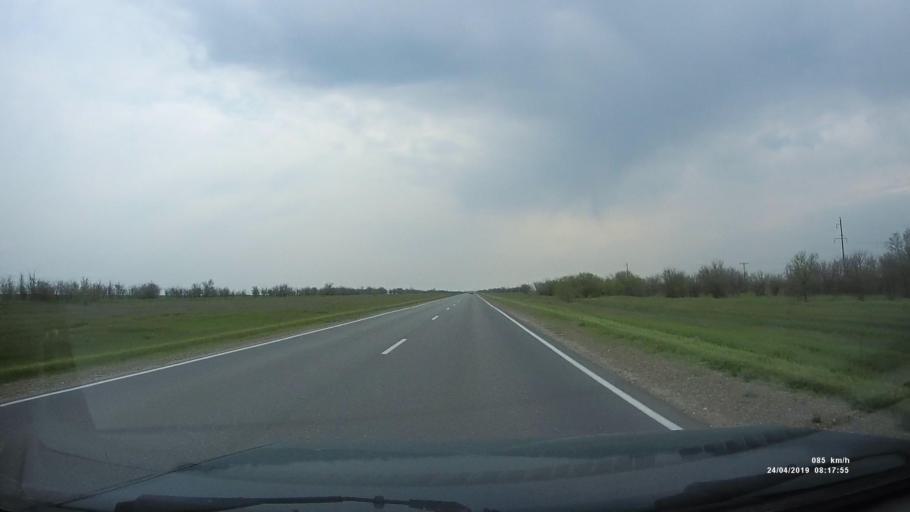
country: RU
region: Kalmykiya
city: Priyutnoye
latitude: 46.0989
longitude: 43.6383
